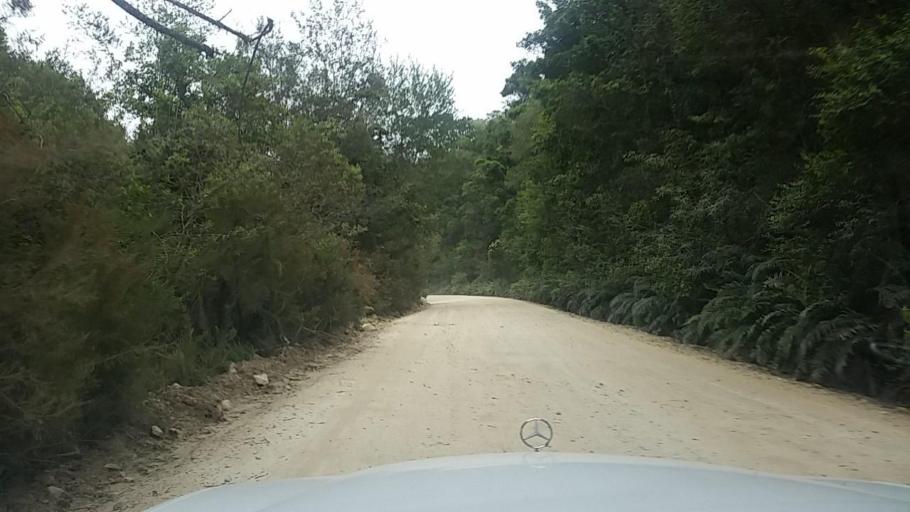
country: ZA
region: Western Cape
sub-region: Eden District Municipality
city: Knysna
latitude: -33.9701
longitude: 23.1473
